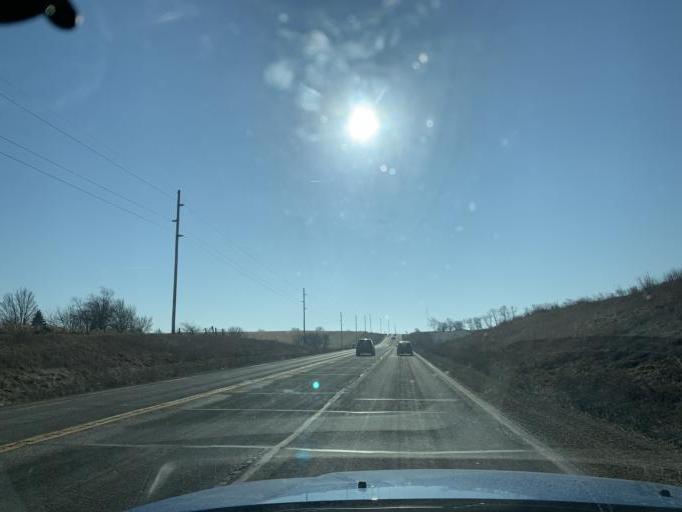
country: US
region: Wisconsin
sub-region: Green County
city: Monticello
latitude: 42.6802
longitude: -89.6169
